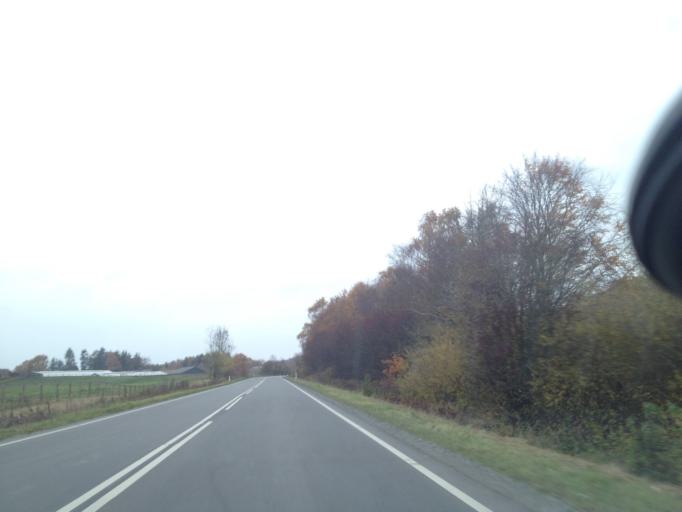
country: DK
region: South Denmark
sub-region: Nordfyns Kommune
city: Sonderso
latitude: 55.4332
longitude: 10.2381
